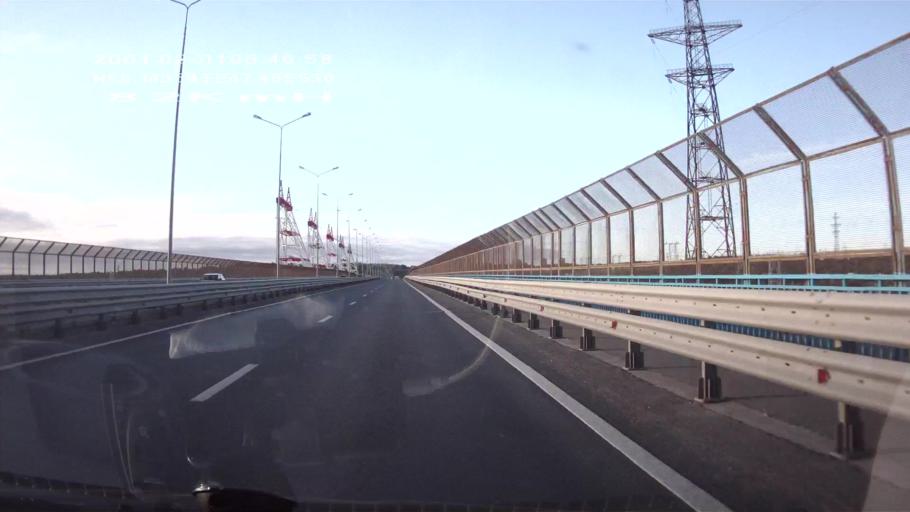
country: RU
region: Chuvashia
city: Novocheboksarsk
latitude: 56.1429
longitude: 47.4655
